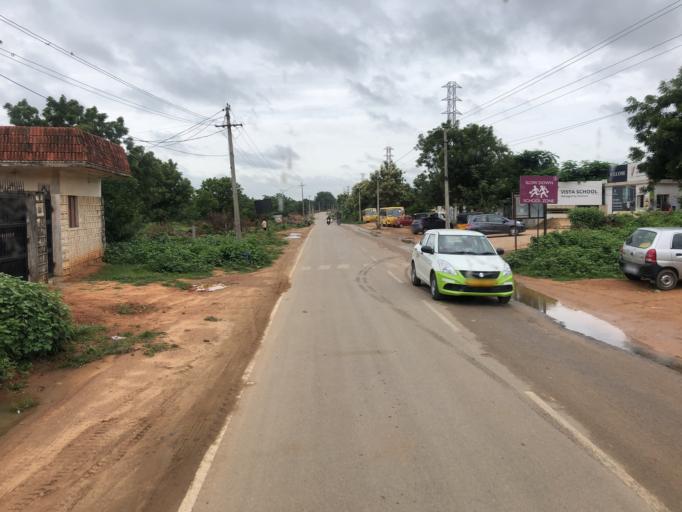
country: IN
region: Telangana
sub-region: Medak
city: Serilingampalle
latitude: 17.4343
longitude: 78.2991
